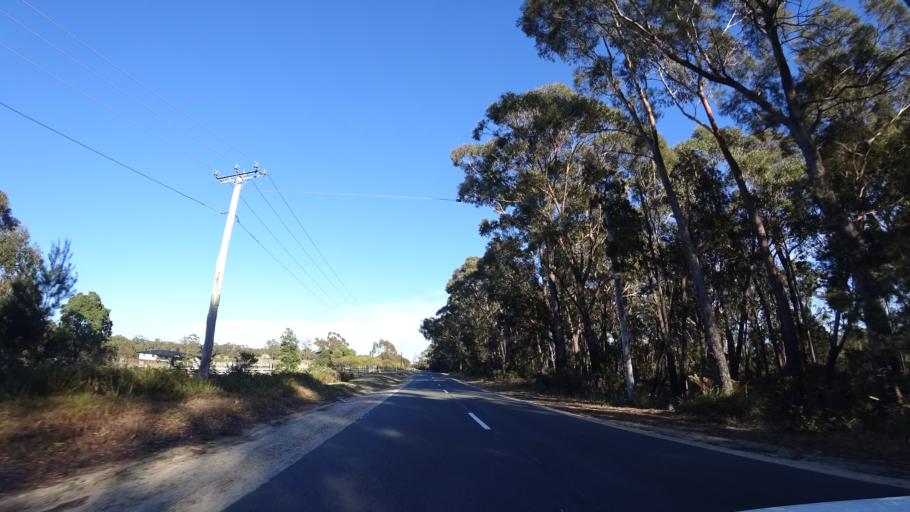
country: AU
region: Tasmania
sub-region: Break O'Day
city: St Helens
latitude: -41.3018
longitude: 148.2128
